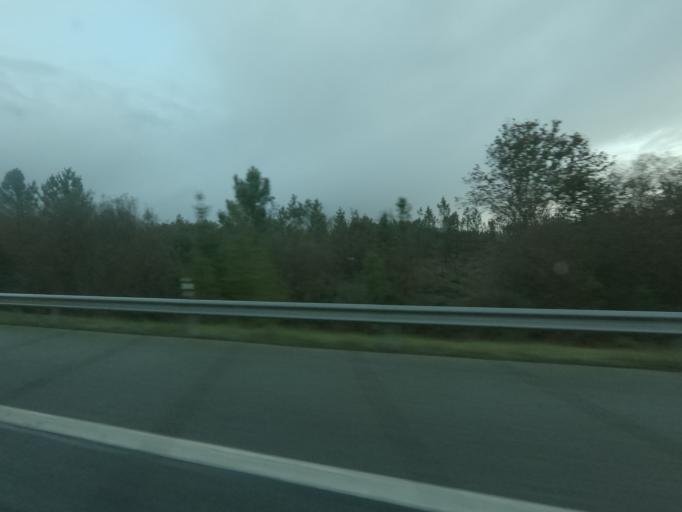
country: PT
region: Braga
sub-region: Vila Verde
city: Prado
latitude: 41.5475
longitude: -8.5052
